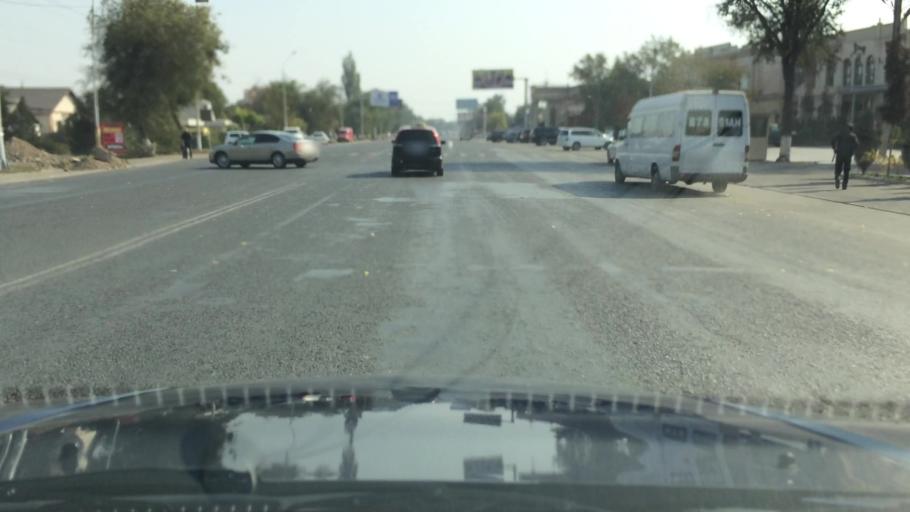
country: KG
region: Chuy
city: Lebedinovka
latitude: 42.8882
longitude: 74.6602
